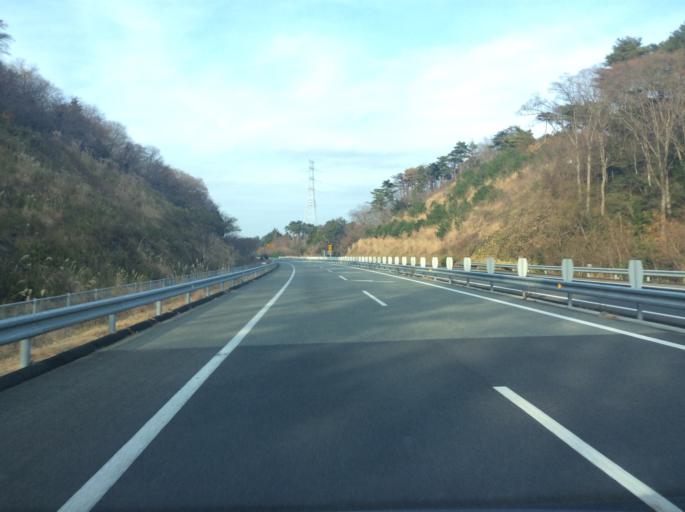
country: JP
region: Fukushima
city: Namie
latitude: 37.3113
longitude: 140.9925
